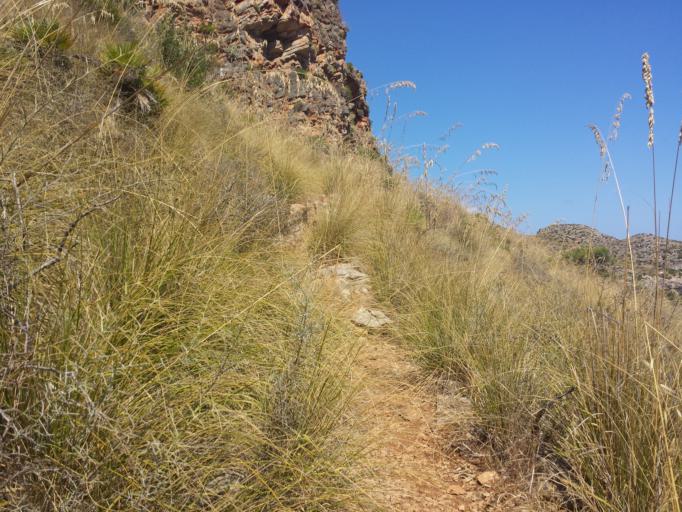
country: IT
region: Sicily
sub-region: Trapani
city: Castellammare del Golfo
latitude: 38.0498
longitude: 12.8539
